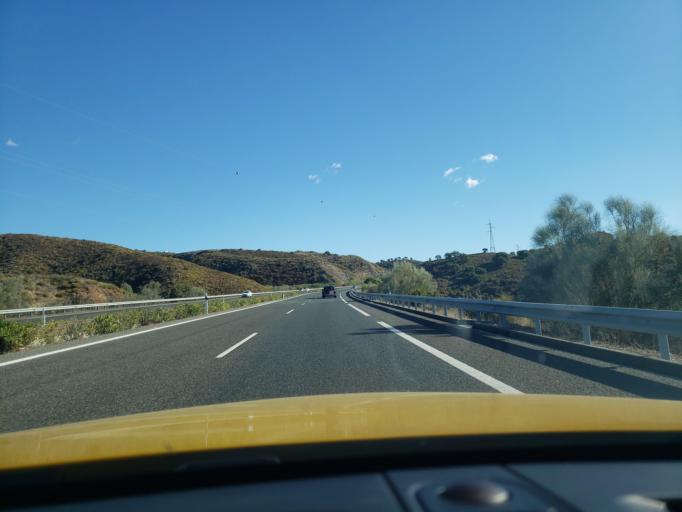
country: ES
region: Andalusia
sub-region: Provincia de Malaga
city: Ojen
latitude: 36.5166
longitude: -4.8125
